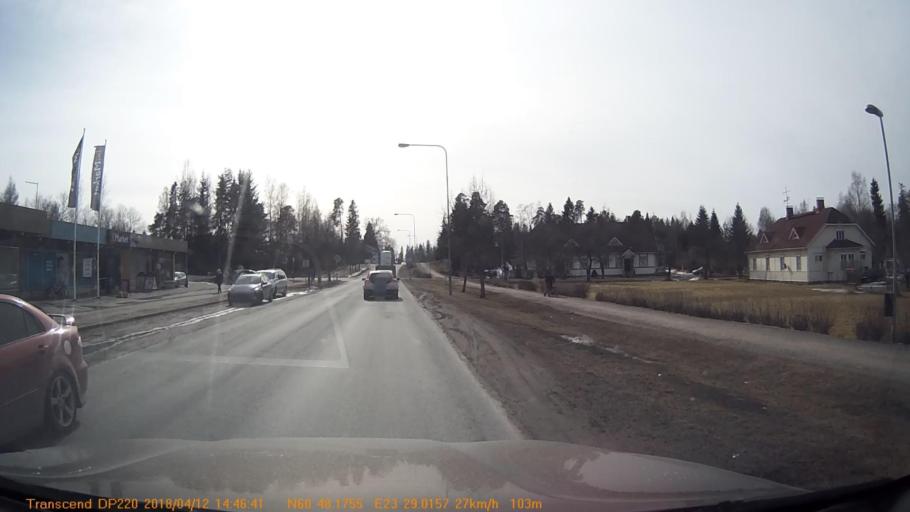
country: FI
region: Haeme
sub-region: Forssa
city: Jokioinen
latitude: 60.8030
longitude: 23.4836
